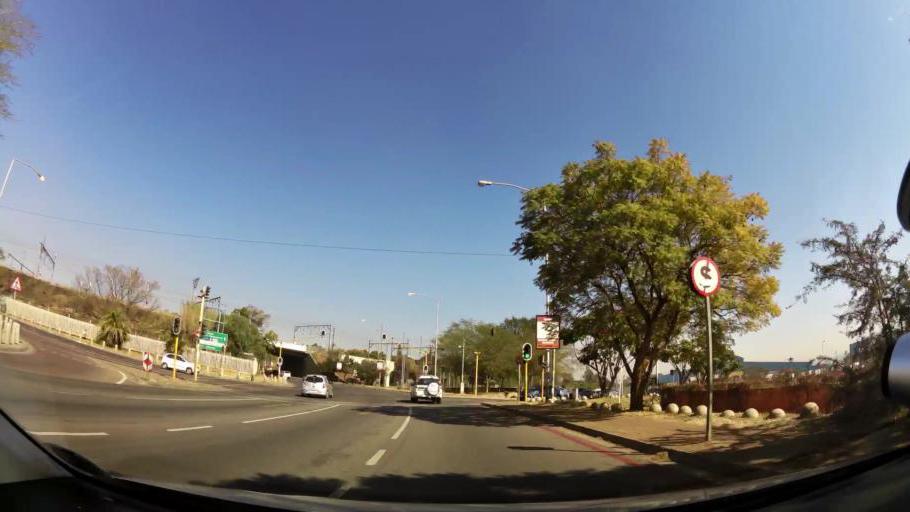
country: ZA
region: Gauteng
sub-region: City of Tshwane Metropolitan Municipality
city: Pretoria
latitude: -25.7549
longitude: 28.1825
